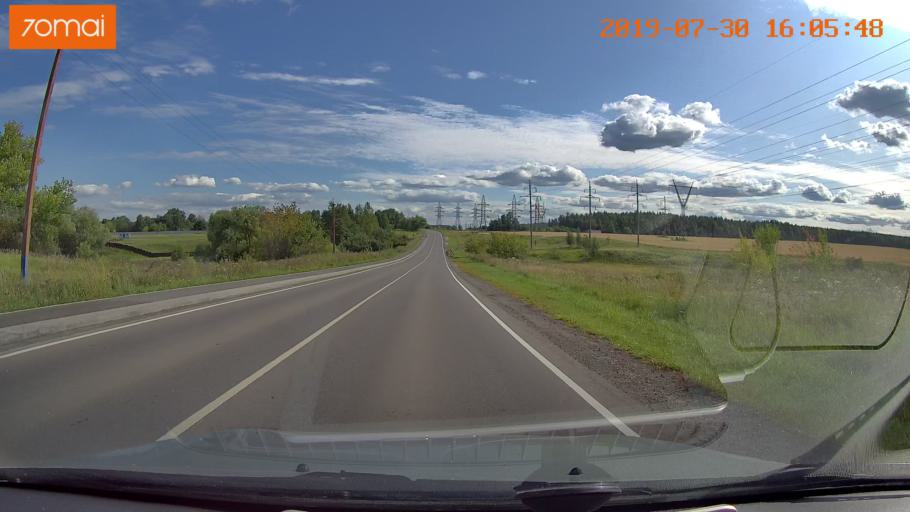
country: RU
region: Moskovskaya
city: Peski
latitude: 55.2618
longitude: 38.7156
